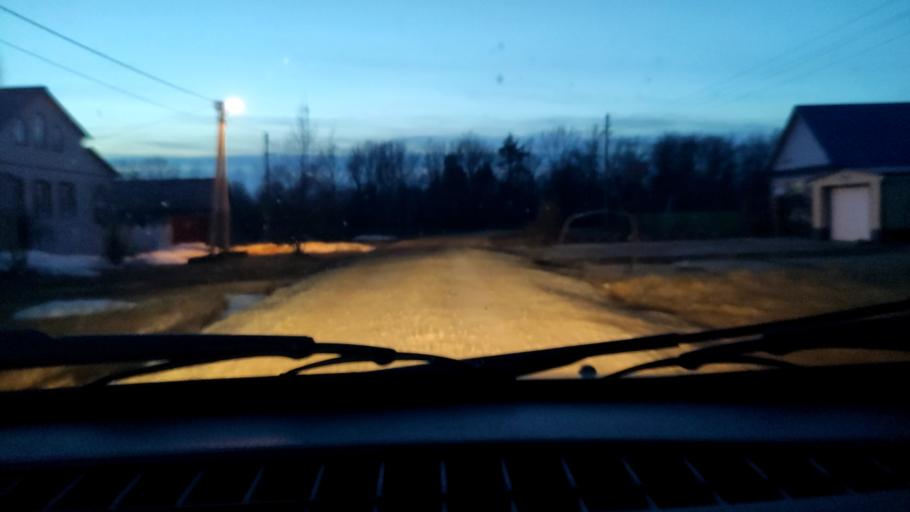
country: RU
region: Bashkortostan
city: Iglino
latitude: 54.7940
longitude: 56.3099
